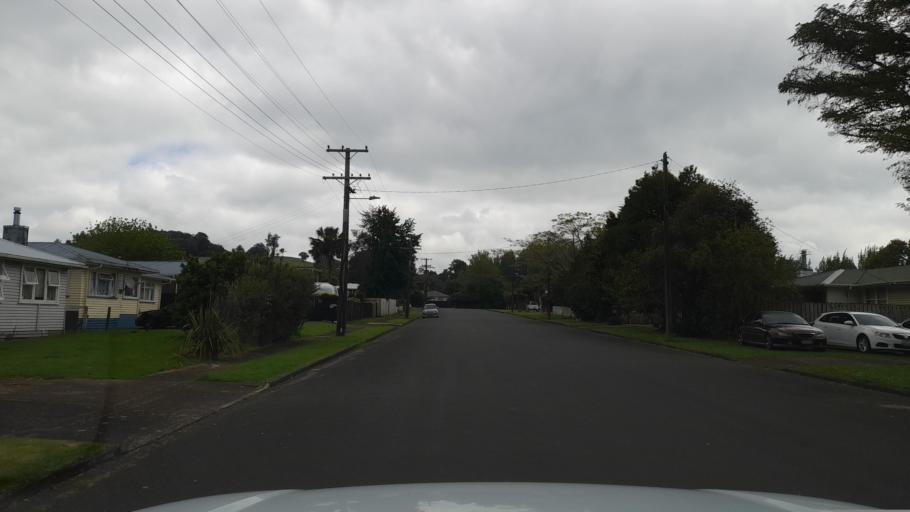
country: NZ
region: Northland
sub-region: Far North District
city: Waimate North
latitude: -35.4035
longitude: 173.7897
